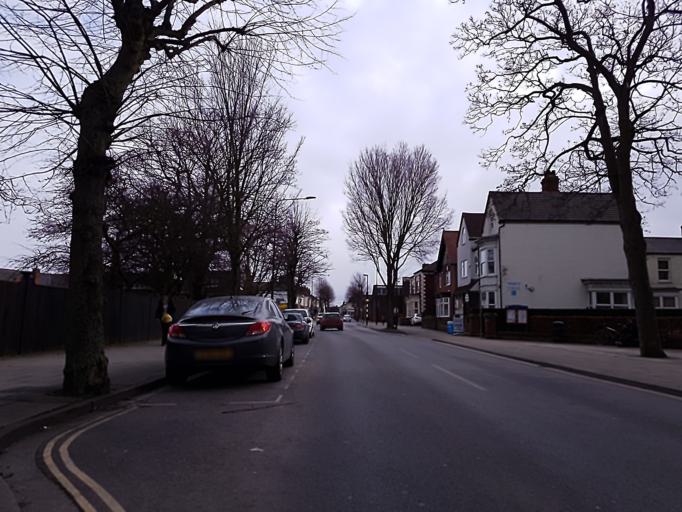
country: GB
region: England
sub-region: North East Lincolnshire
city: Cleethorpes
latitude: 53.5583
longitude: -0.0304
